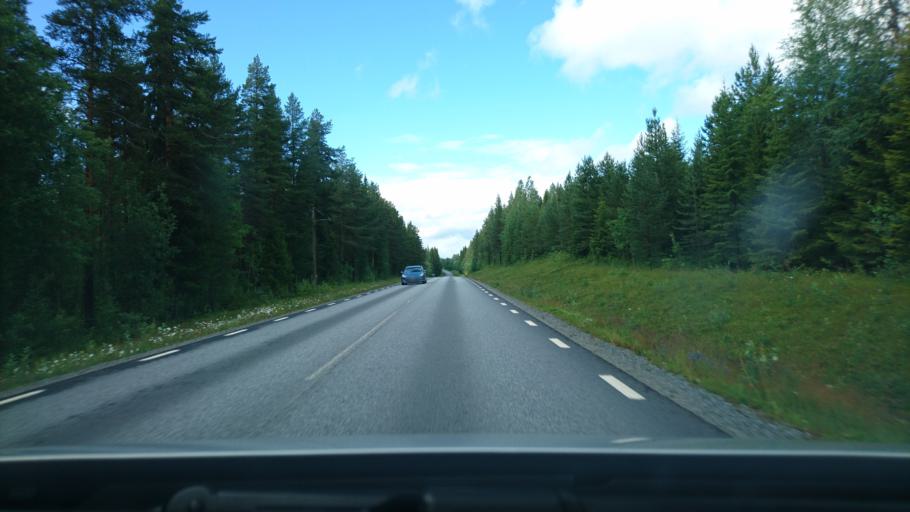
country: SE
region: Vaesterbotten
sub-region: Vilhelmina Kommun
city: Vilhelmina
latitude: 64.5633
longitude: 16.7418
